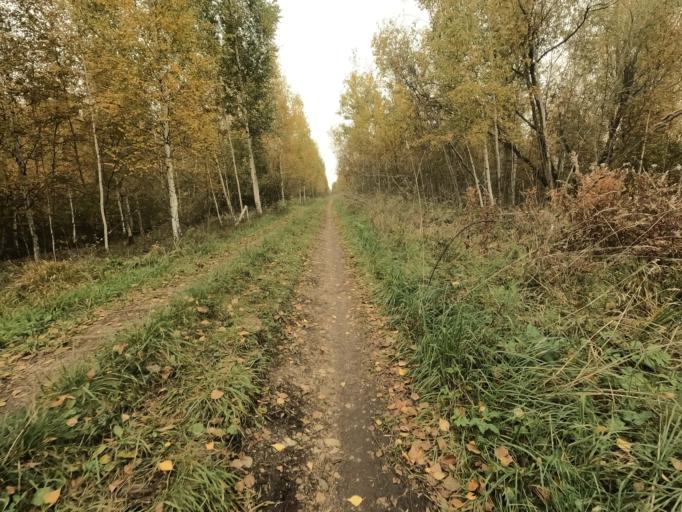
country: RU
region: Novgorod
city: Pankovka
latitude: 58.8866
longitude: 30.9470
